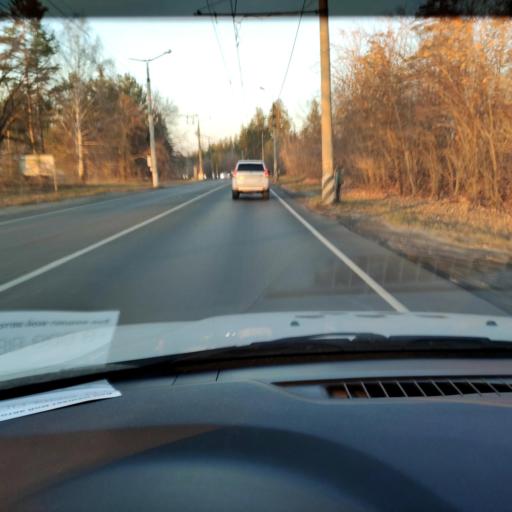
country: RU
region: Samara
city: Tol'yatti
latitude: 53.4885
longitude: 49.3838
